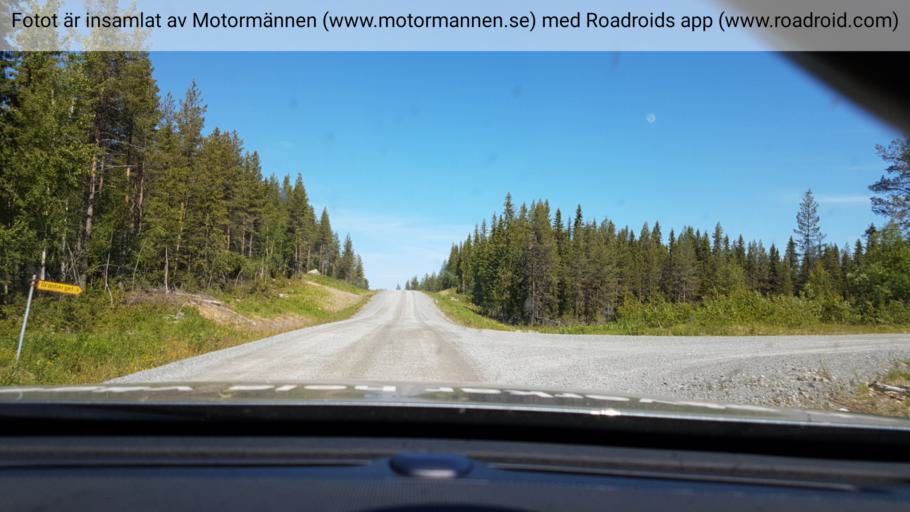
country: SE
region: Vaesterbotten
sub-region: Vilhelmina Kommun
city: Sjoberg
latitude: 64.6703
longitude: 15.7578
